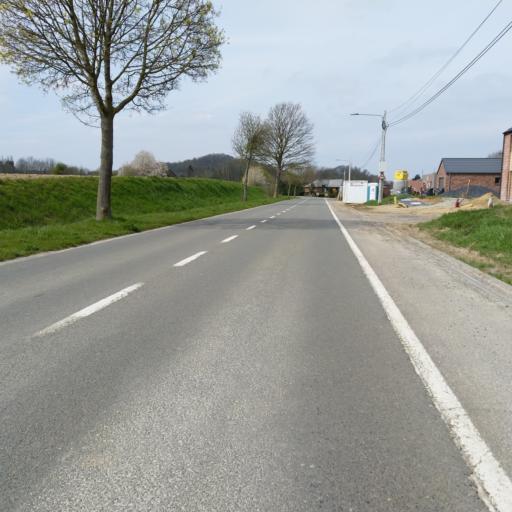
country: BE
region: Wallonia
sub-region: Province du Hainaut
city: Quevy-le-Petit
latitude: 50.3886
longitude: 3.9180
